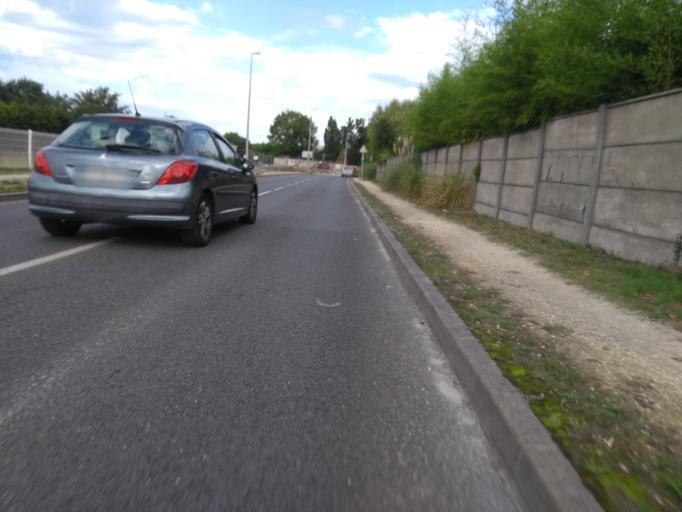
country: FR
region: Aquitaine
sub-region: Departement de la Gironde
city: Cestas
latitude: 44.7851
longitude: -0.6806
